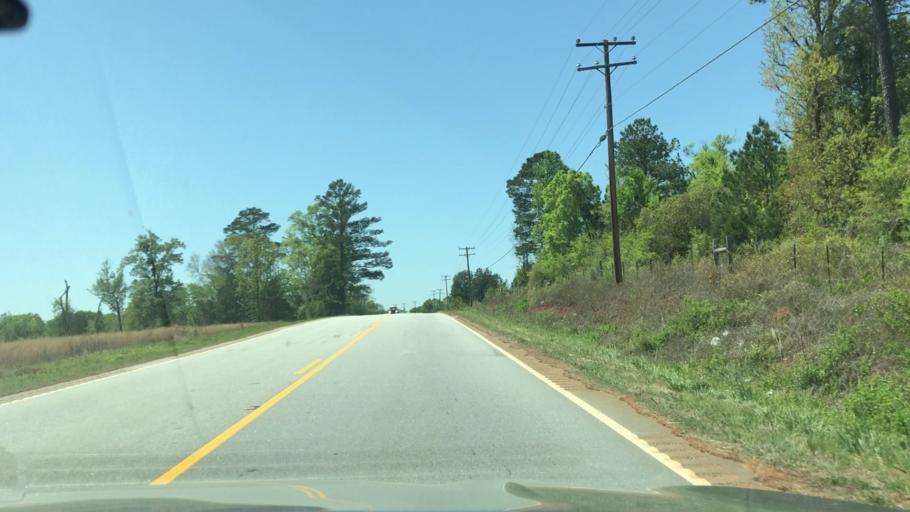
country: US
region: South Carolina
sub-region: Union County
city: Buffalo
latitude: 34.6836
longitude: -81.7191
